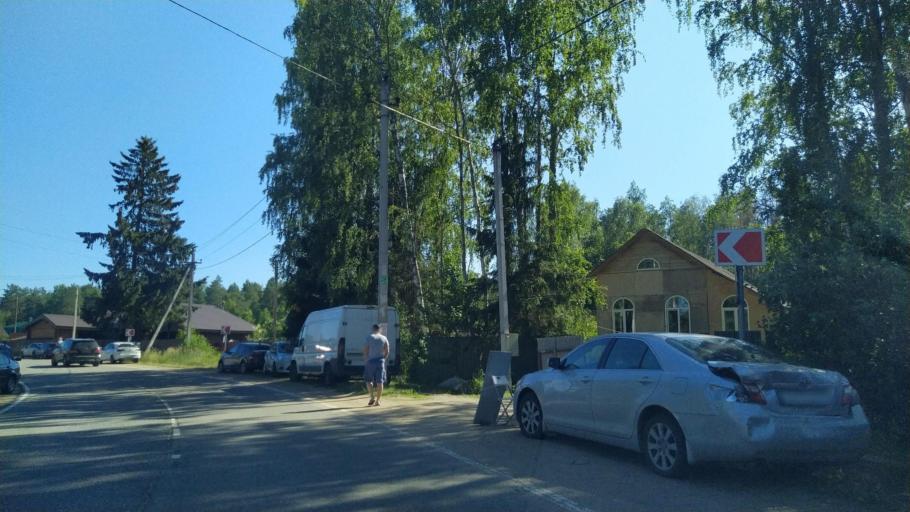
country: RU
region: Leningrad
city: Borisova Griva
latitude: 60.1208
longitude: 31.0740
